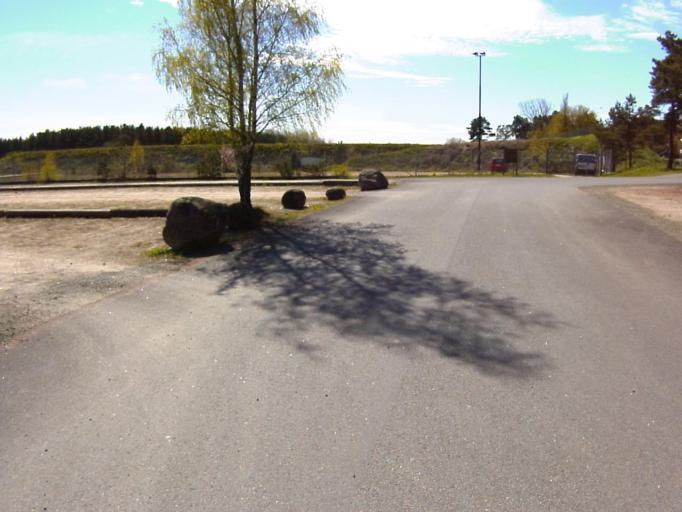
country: SE
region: Skane
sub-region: Kristianstads Kommun
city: Norra Asum
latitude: 55.9894
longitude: 14.1466
